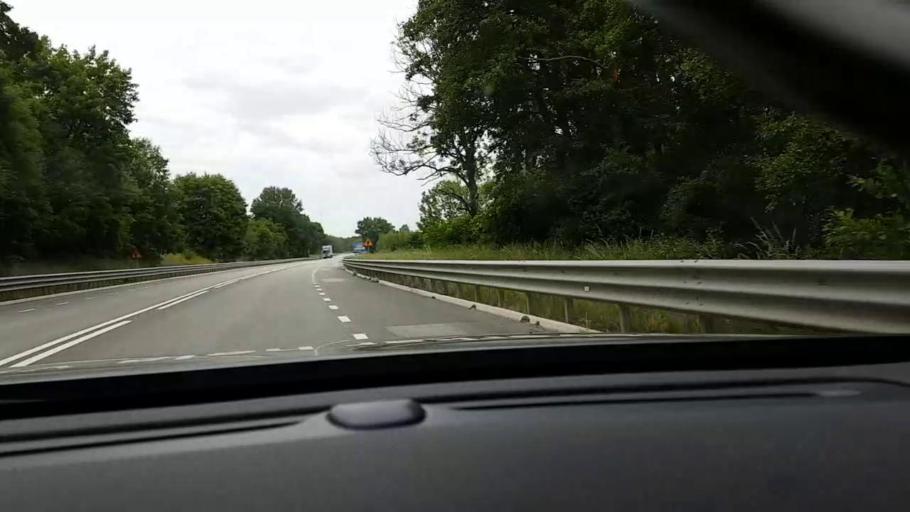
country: SE
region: Skane
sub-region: Hassleholms Kommun
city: Hassleholm
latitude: 56.1457
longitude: 13.8042
